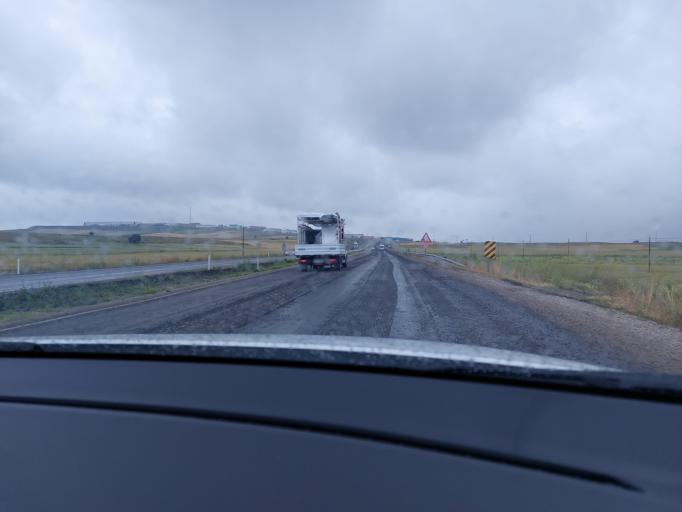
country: TR
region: Nevsehir
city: Dobada
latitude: 38.5388
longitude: 34.4523
